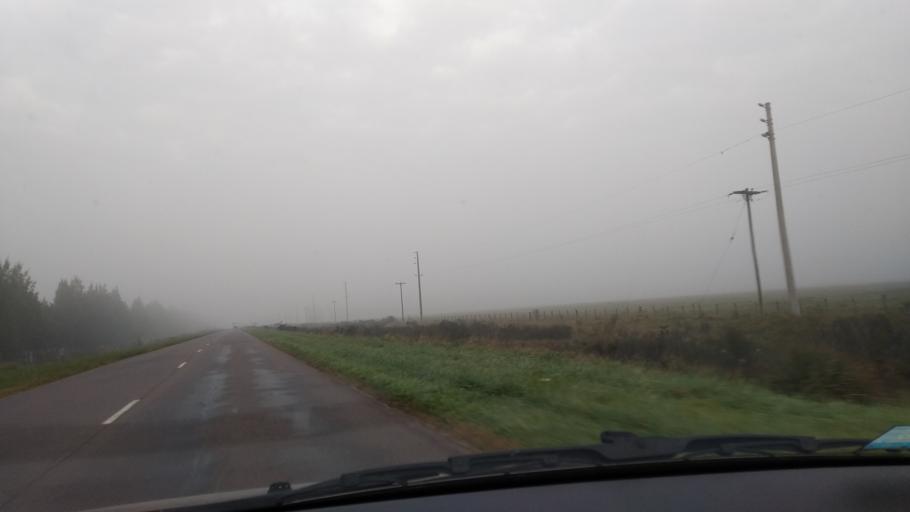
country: AR
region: Buenos Aires
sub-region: Partido de San Vicente
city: San Vicente
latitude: -35.2545
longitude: -58.5028
